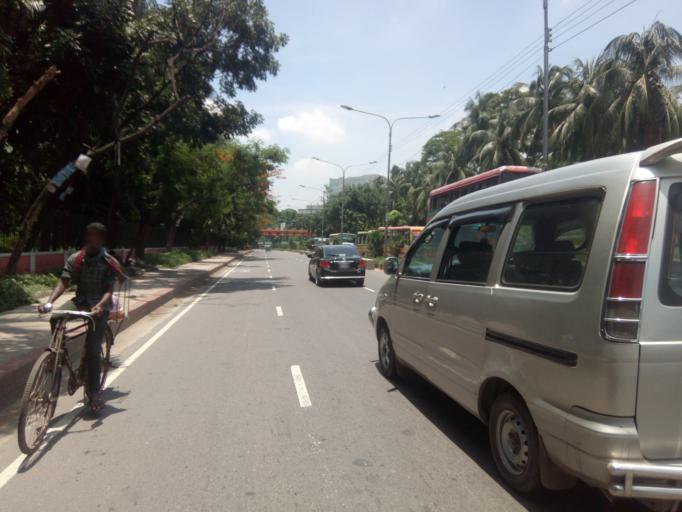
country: BD
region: Dhaka
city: Paltan
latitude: 23.7362
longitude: 90.4001
